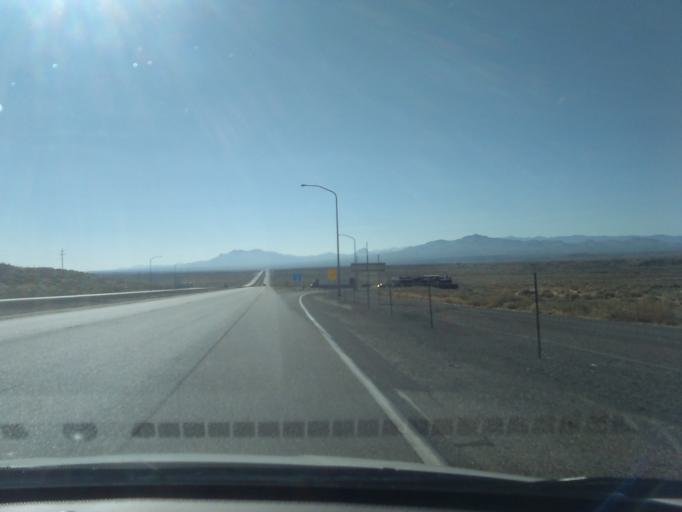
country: US
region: New Mexico
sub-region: Socorro County
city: Socorro
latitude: 34.3079
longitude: -106.8890
